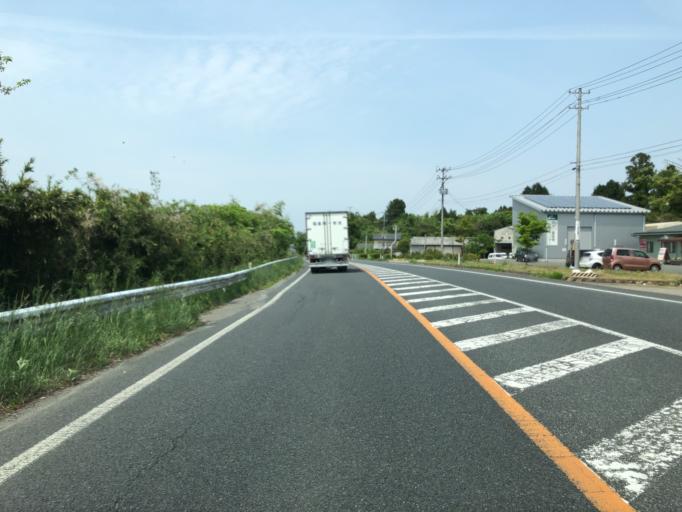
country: JP
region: Miyagi
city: Marumori
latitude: 37.8175
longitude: 140.9220
